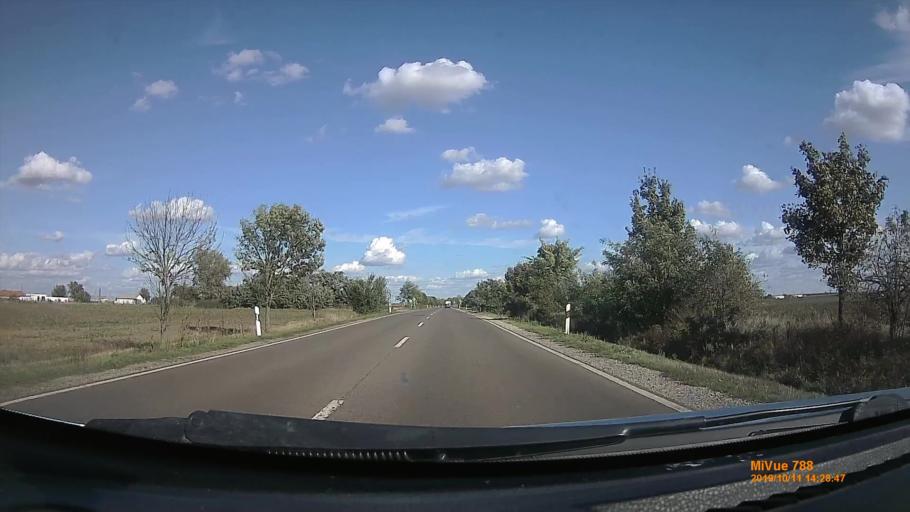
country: HU
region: Hajdu-Bihar
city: Balmazujvaros
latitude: 47.5577
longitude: 21.3728
